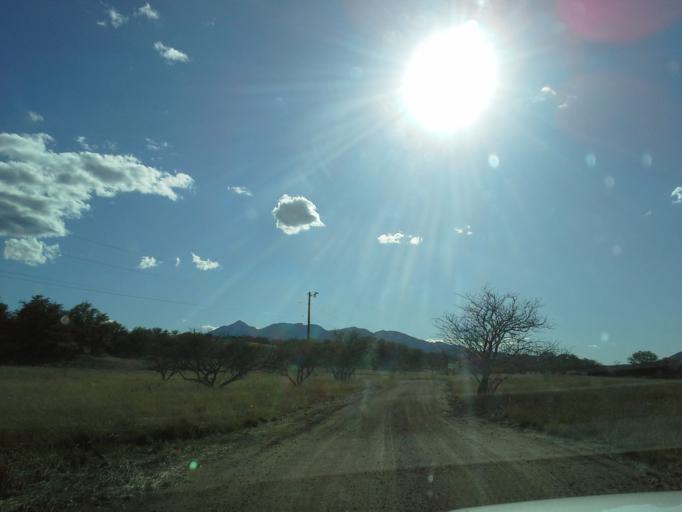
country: US
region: Arizona
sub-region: Pima County
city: Corona de Tucson
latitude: 31.7432
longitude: -110.7064
